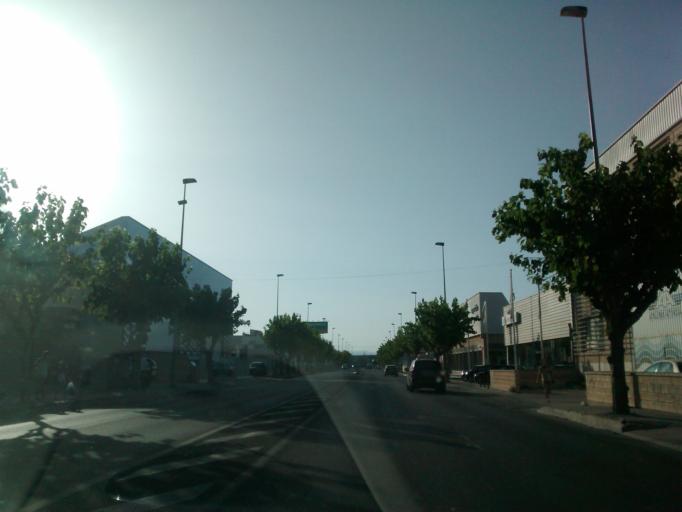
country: ES
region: Valencia
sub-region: Provincia de Alicante
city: Santa Pola
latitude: 38.1978
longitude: -0.5644
